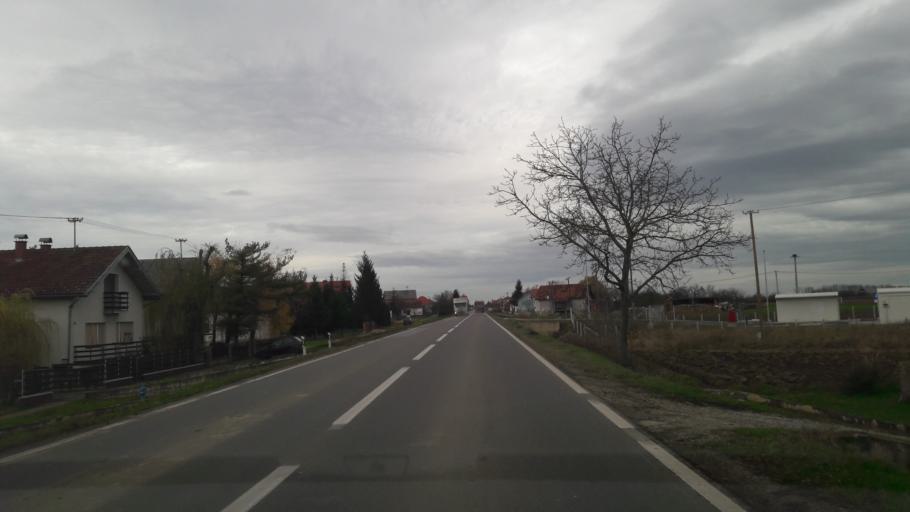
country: HR
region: Osjecko-Baranjska
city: Fericanci
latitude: 45.5268
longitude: 17.9607
